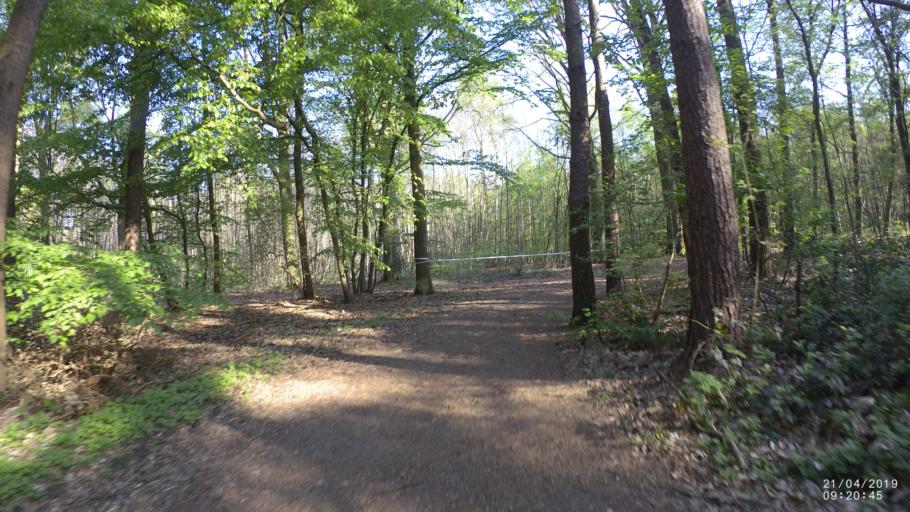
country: BE
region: Flanders
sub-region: Provincie Vlaams-Brabant
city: Lubbeek
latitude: 50.9149
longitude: 4.8542
